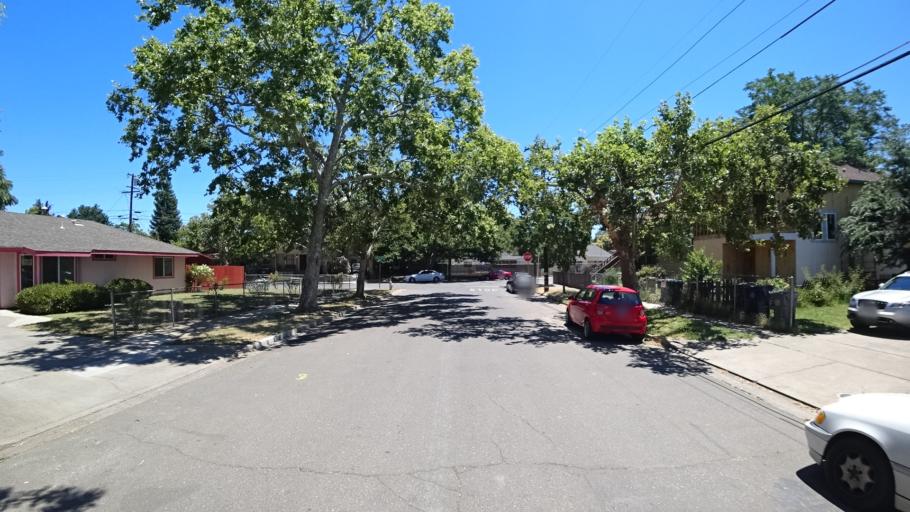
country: US
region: California
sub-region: Sacramento County
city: Sacramento
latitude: 38.5495
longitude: -121.4607
